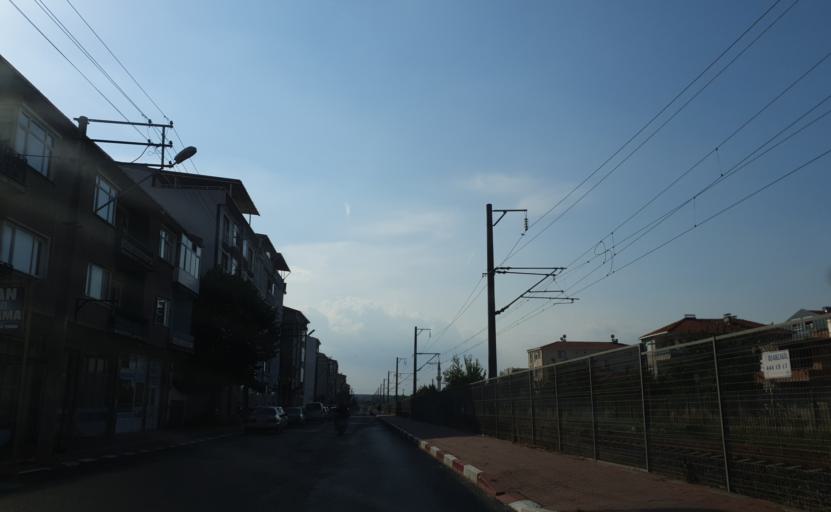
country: TR
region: Tekirdag
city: Muratli
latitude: 41.1734
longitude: 27.4955
